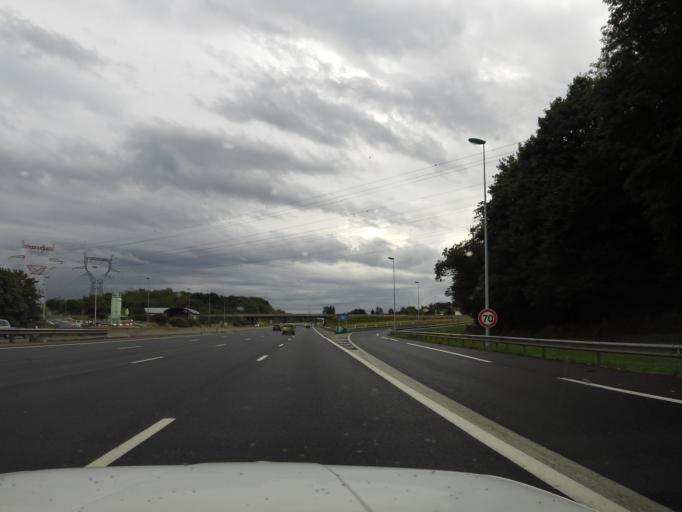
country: FR
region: Rhone-Alpes
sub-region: Departement de l'Isere
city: Grenay
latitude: 45.6543
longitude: 5.0956
